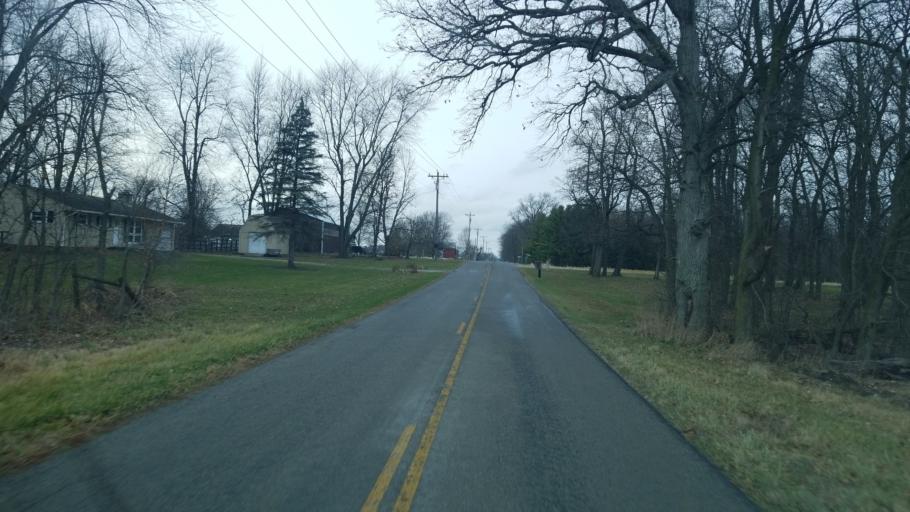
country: US
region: Ohio
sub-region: Union County
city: Marysville
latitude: 40.2927
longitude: -83.2728
